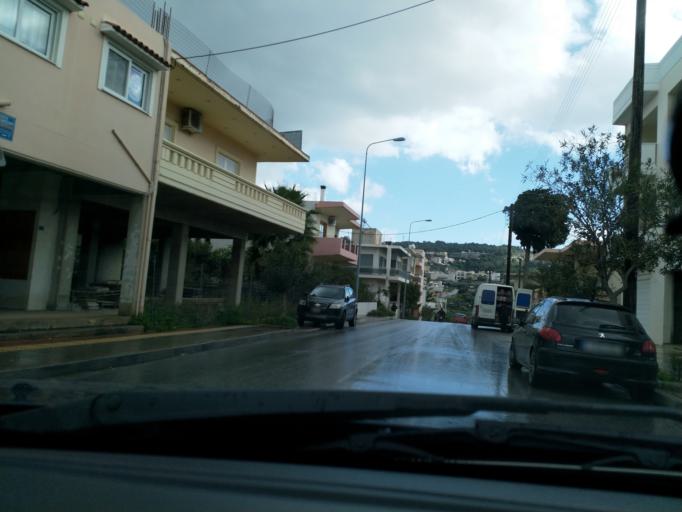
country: GR
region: Crete
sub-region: Nomos Chanias
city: Chania
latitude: 35.5118
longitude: 24.0422
